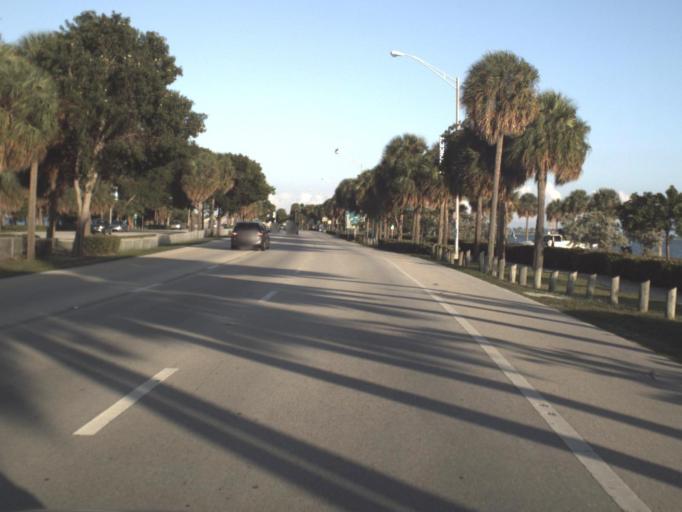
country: US
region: Florida
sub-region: Miami-Dade County
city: Miami
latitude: 25.7459
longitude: -80.1970
